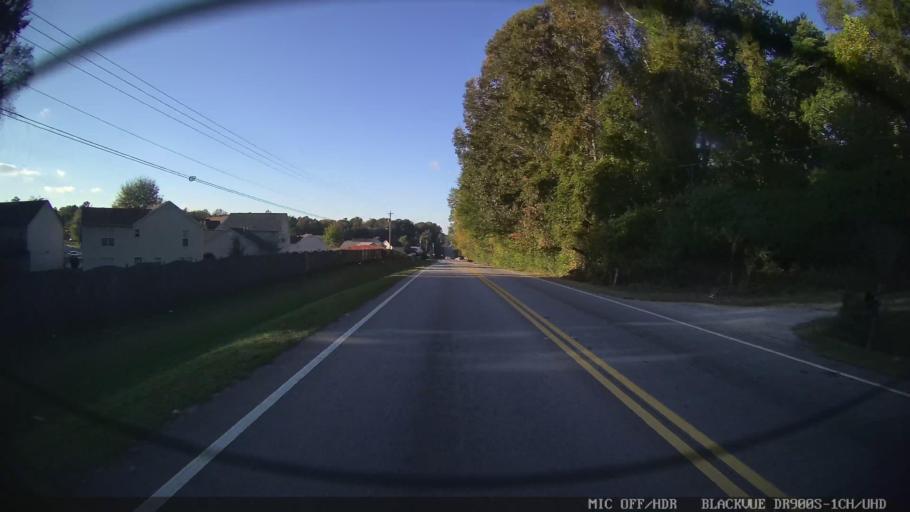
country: US
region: Georgia
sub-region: Clayton County
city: Lake City
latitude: 33.5961
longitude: -84.2962
